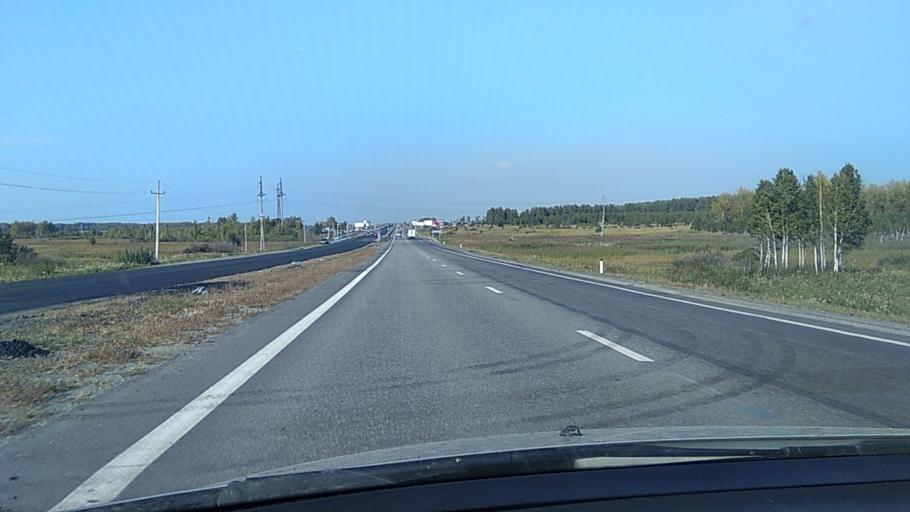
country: RU
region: Chelyabinsk
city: Sargazy
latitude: 55.0381
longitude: 61.3010
